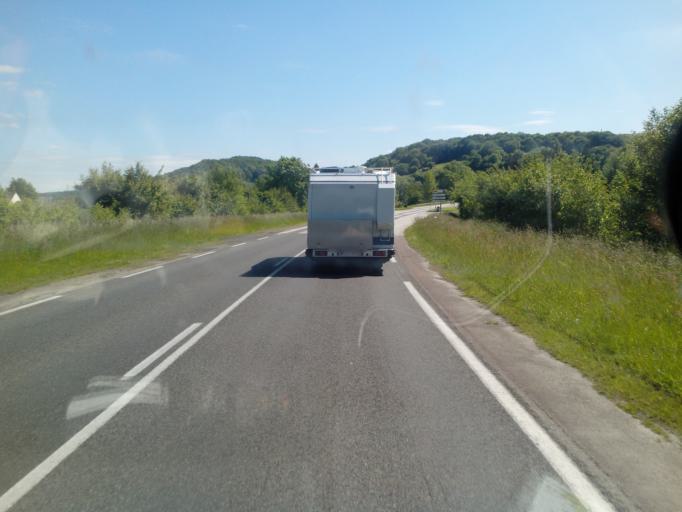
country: FR
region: Haute-Normandie
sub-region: Departement de l'Eure
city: Toutainville
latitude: 49.4032
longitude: 0.4259
